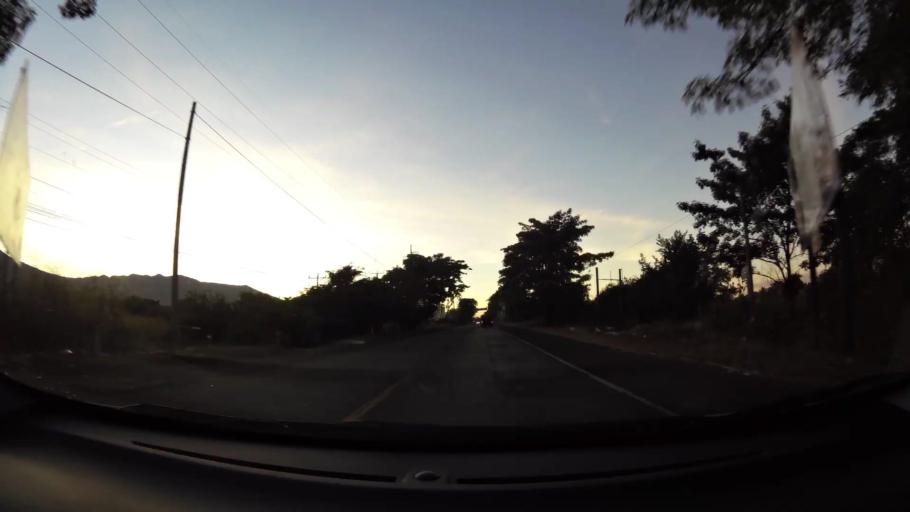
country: SV
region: San Miguel
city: Moncagua
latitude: 13.5049
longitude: -88.2278
